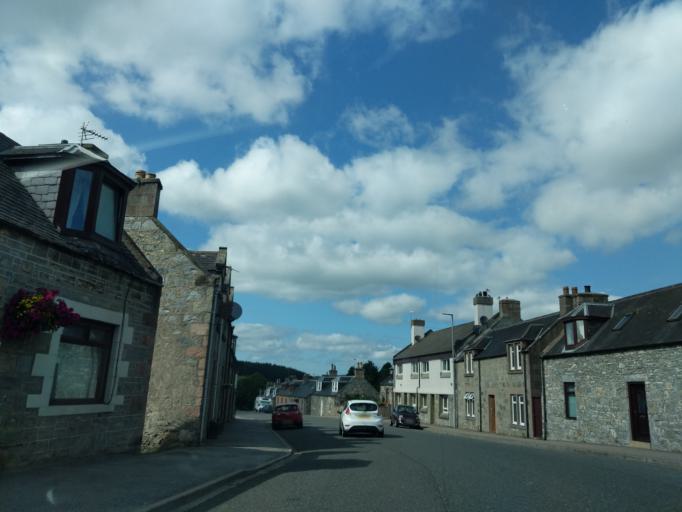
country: GB
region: Scotland
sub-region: Moray
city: Dufftown
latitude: 57.4478
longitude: -3.1292
